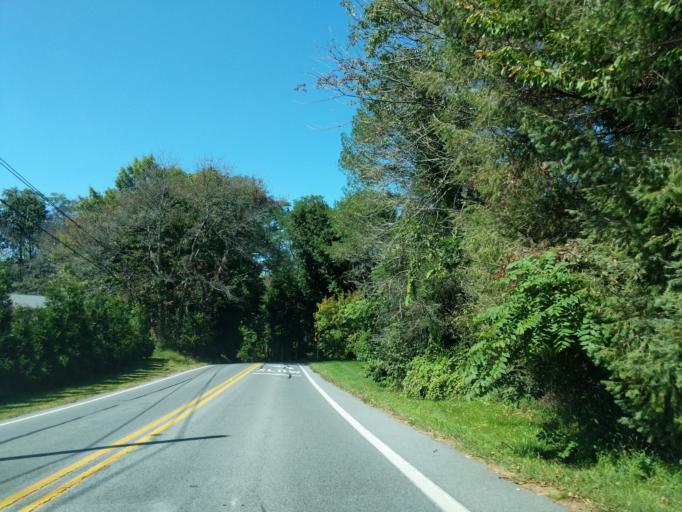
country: US
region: Pennsylvania
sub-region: Montgomery County
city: East Greenville
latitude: 40.4491
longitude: -75.4899
